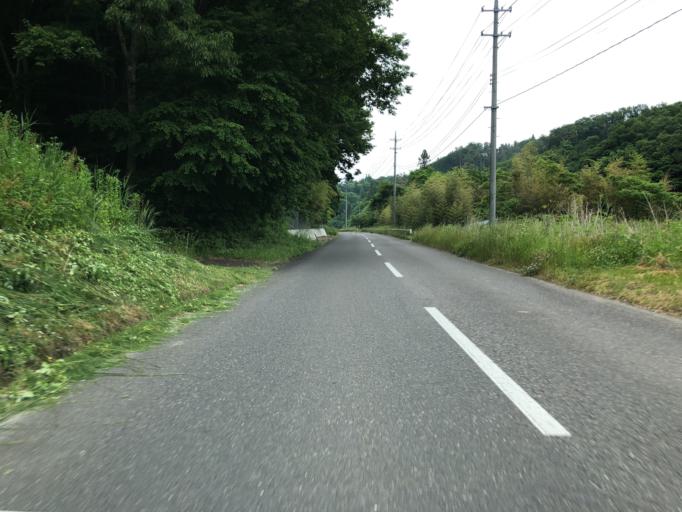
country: JP
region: Fukushima
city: Funehikimachi-funehiki
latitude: 37.4260
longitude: 140.6137
